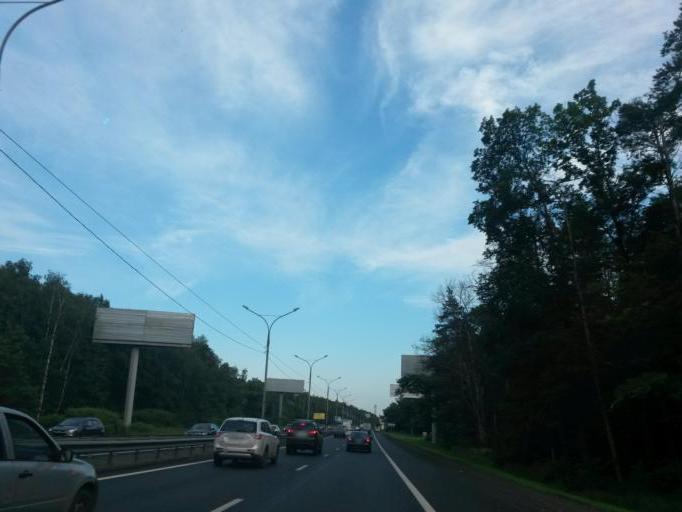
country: RU
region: Moskovskaya
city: Petrovskaya
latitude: 55.5427
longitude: 37.8007
